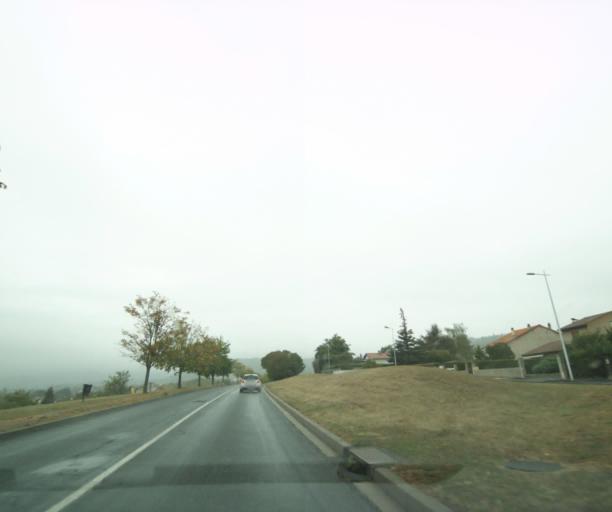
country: FR
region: Auvergne
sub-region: Departement du Puy-de-Dome
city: Cebazat
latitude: 45.8354
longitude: 3.1001
